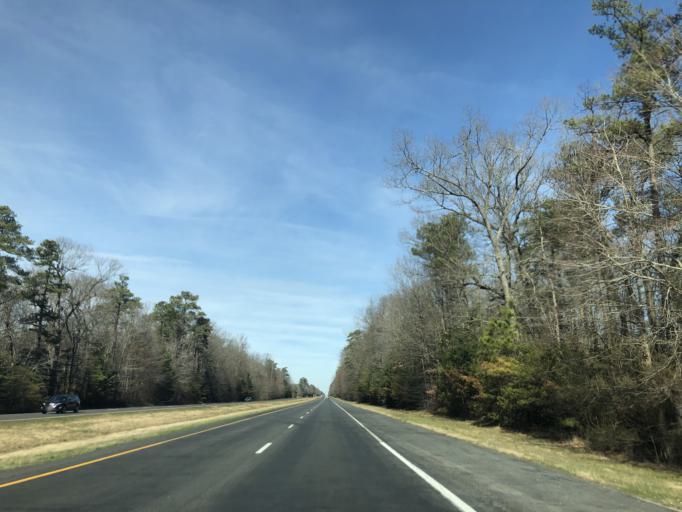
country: US
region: Delaware
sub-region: Sussex County
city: Georgetown
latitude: 38.7640
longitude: -75.4382
